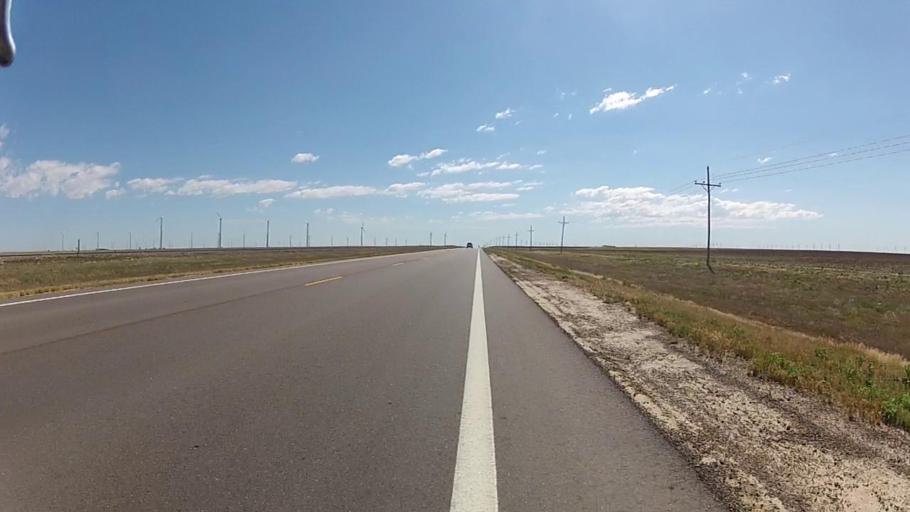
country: US
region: Kansas
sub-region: Gray County
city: Cimarron
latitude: 37.6056
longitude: -100.4203
